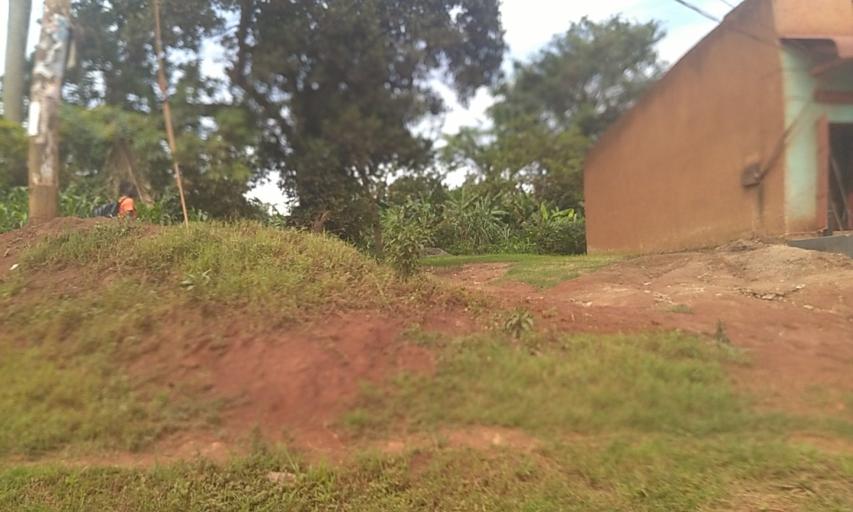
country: UG
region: Central Region
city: Kampala Central Division
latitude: 0.2818
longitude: 32.5175
